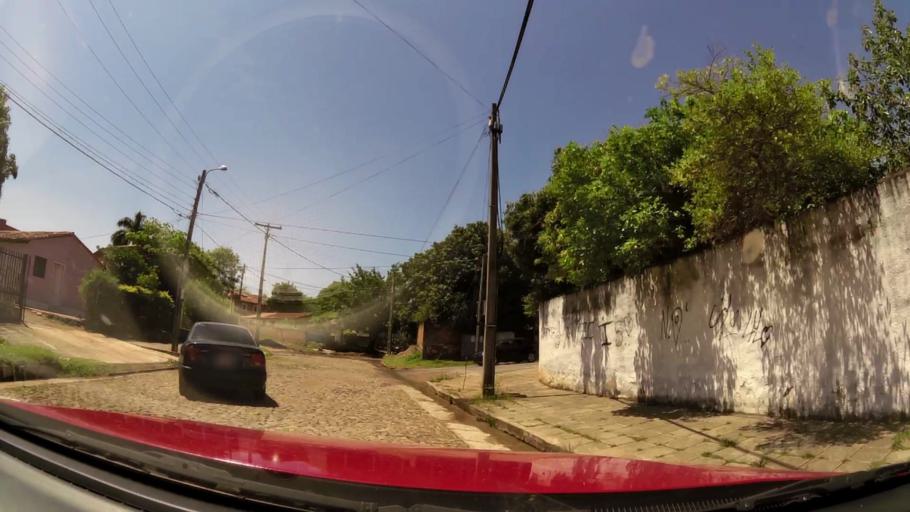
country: PY
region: Central
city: Colonia Mariano Roque Alonso
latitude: -25.2361
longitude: -57.5482
